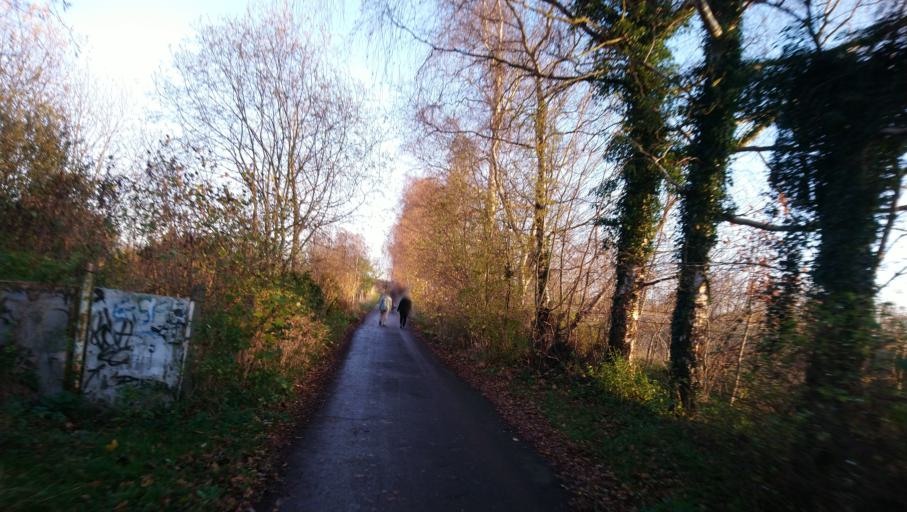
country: DE
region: Mecklenburg-Vorpommern
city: Kritzmow
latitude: 54.0659
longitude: 12.0959
